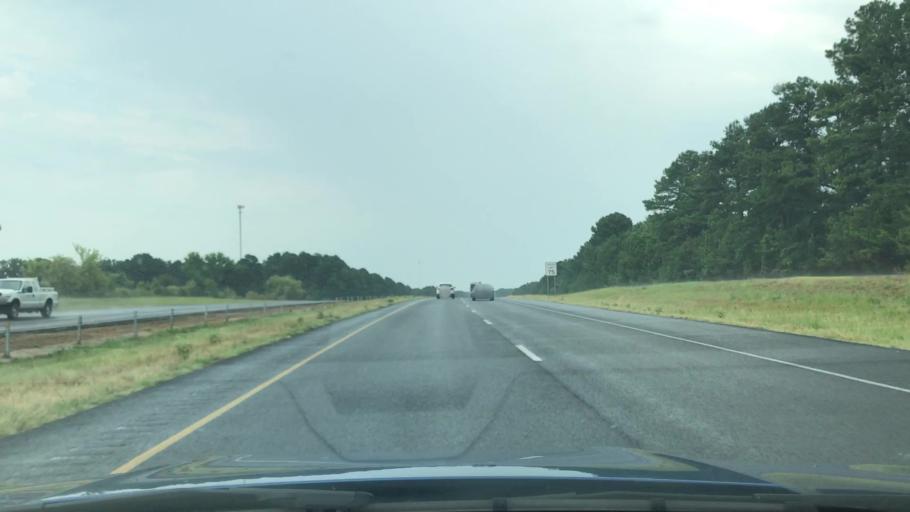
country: US
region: Texas
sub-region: Harrison County
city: Marshall
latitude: 32.4961
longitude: -94.2308
